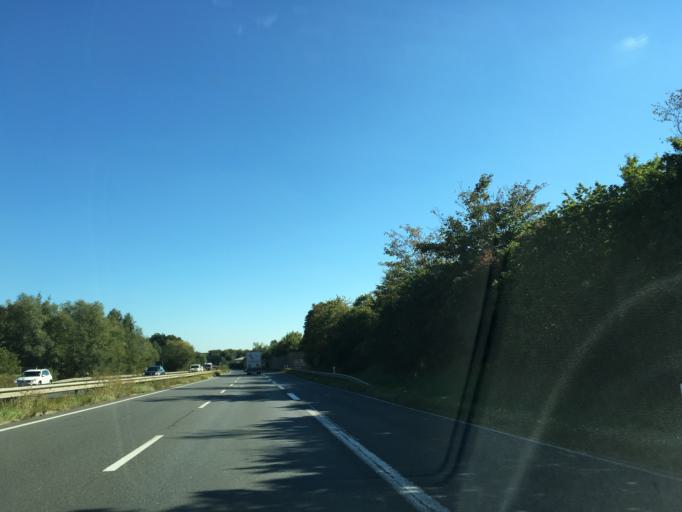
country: DE
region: Lower Saxony
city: Bardowick
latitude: 53.2766
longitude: 10.4042
